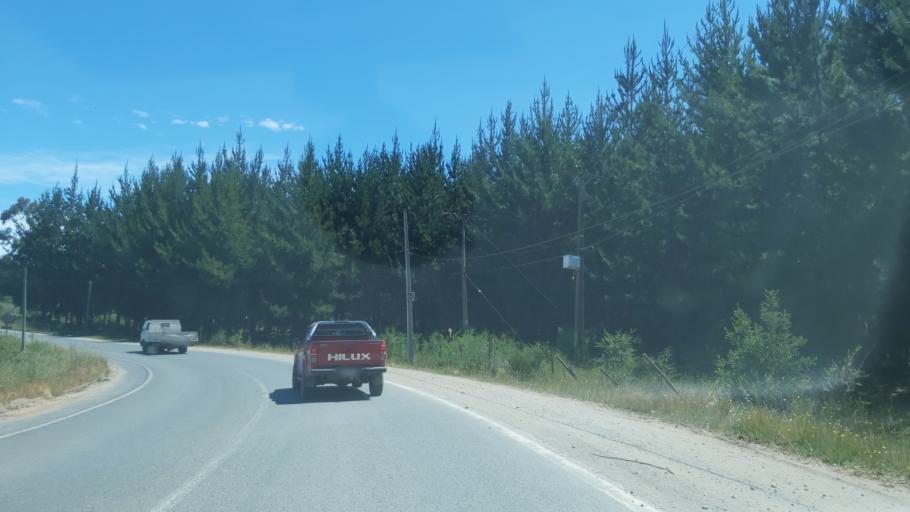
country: CL
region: Maule
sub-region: Provincia de Talca
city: Constitucion
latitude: -35.3987
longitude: -72.4355
